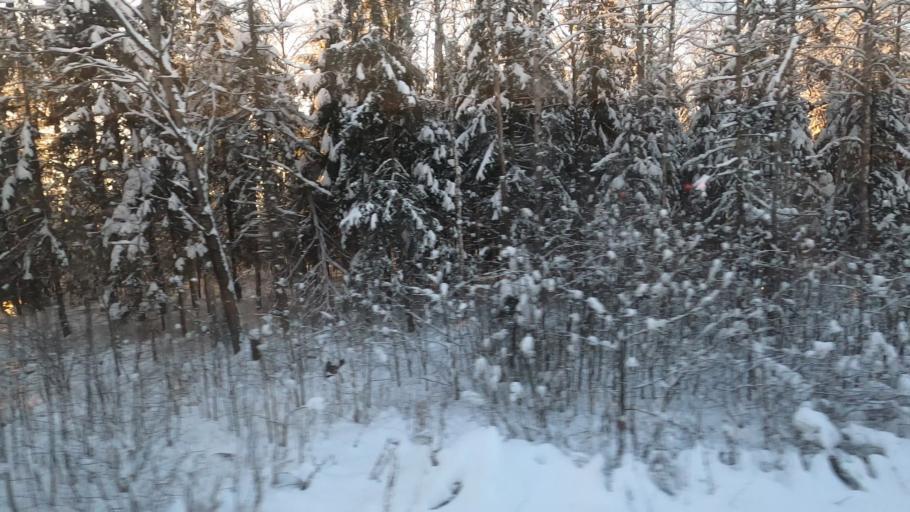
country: RU
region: Moskovskaya
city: Novo-Nikol'skoye
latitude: 56.5856
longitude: 37.5669
